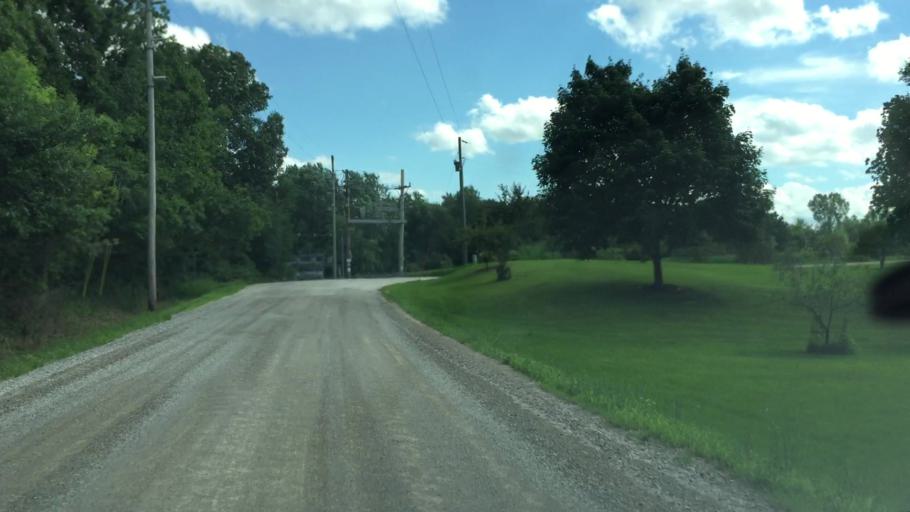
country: US
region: Iowa
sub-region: Linn County
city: Ely
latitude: 41.8290
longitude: -91.6196
